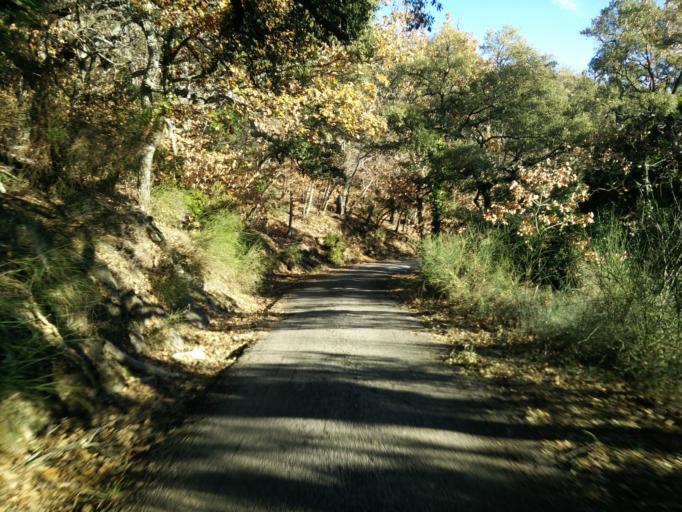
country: FR
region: Provence-Alpes-Cote d'Azur
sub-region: Departement du Var
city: Gonfaron
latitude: 43.2789
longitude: 6.2941
